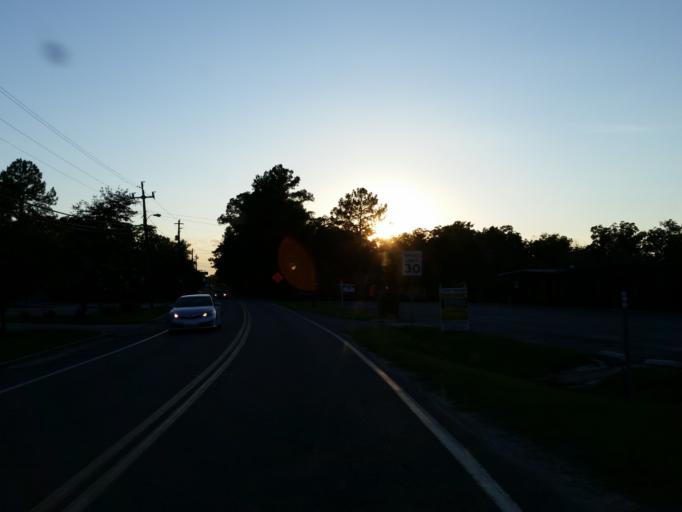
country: US
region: Georgia
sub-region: Berrien County
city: Nashville
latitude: 31.2053
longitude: -83.2439
